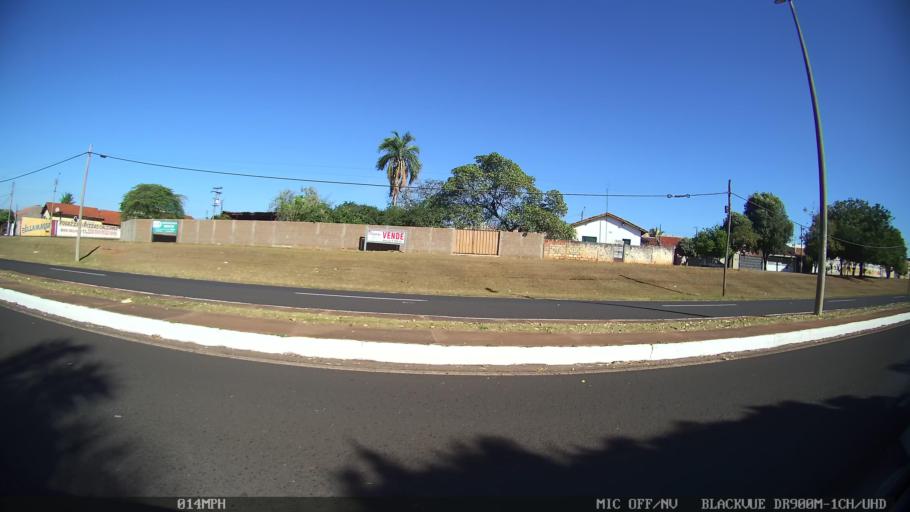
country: BR
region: Sao Paulo
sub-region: Olimpia
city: Olimpia
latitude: -20.7382
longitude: -48.8920
